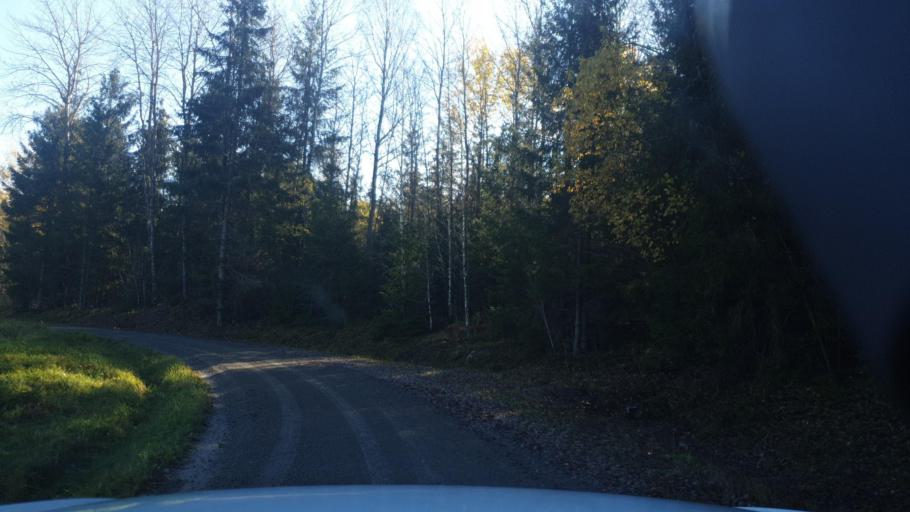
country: SE
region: Vaermland
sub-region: Grums Kommun
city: Grums
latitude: 59.5340
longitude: 12.9066
